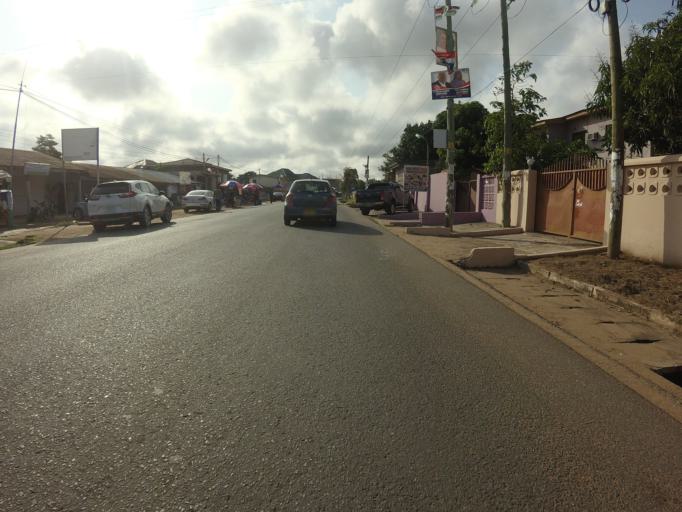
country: GH
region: Greater Accra
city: Nungua
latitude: 5.6150
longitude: -0.0749
